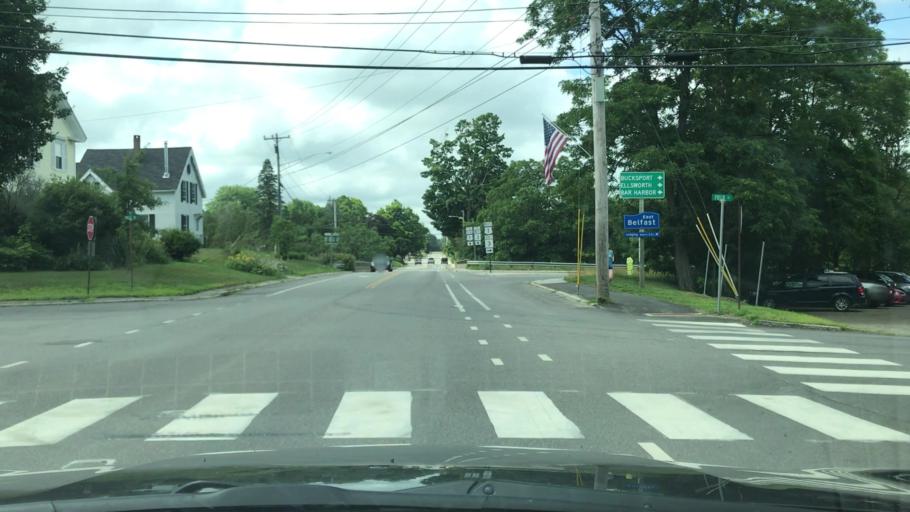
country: US
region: Maine
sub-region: Waldo County
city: Belfast
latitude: 44.4311
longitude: -69.0146
